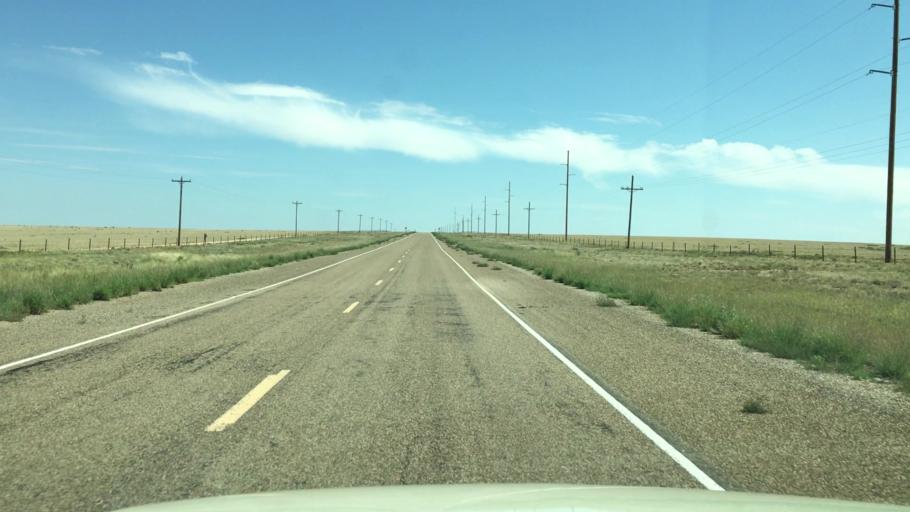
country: US
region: New Mexico
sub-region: Chaves County
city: Roswell
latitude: 33.9404
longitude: -104.5927
